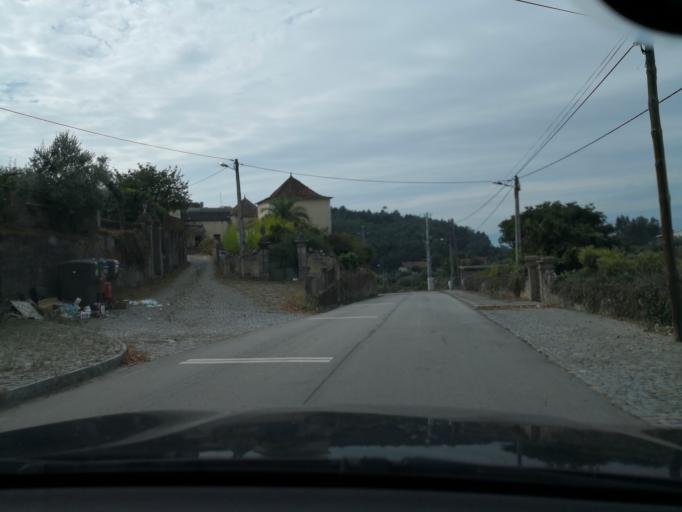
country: PT
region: Vila Real
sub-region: Peso da Regua
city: Peso da Regua
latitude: 41.1997
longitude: -7.7137
